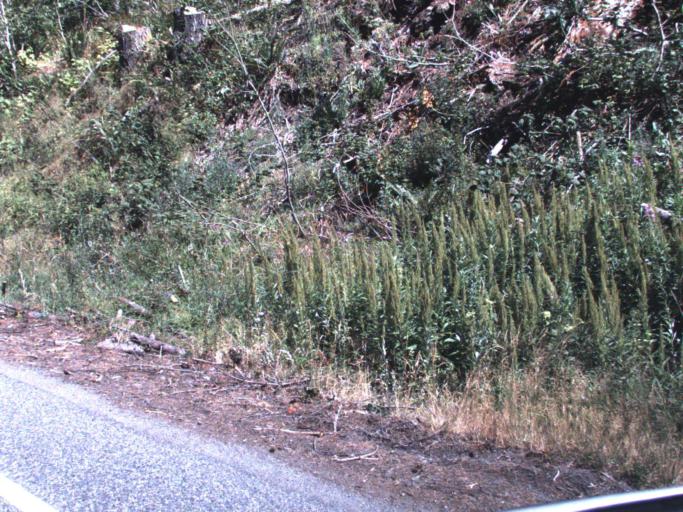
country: US
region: Washington
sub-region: King County
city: Enumclaw
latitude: 47.1658
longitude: -121.7563
